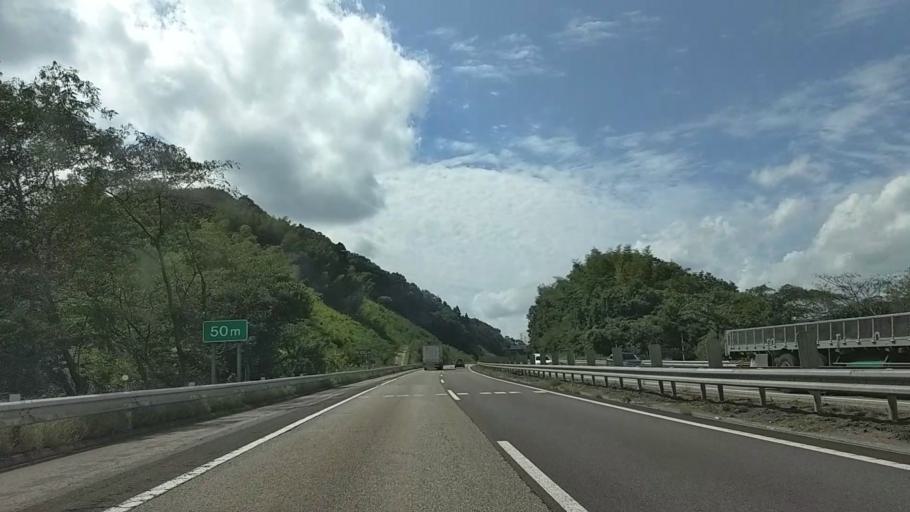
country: JP
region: Toyama
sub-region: Oyabe Shi
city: Oyabe
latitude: 36.6174
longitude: 136.8227
